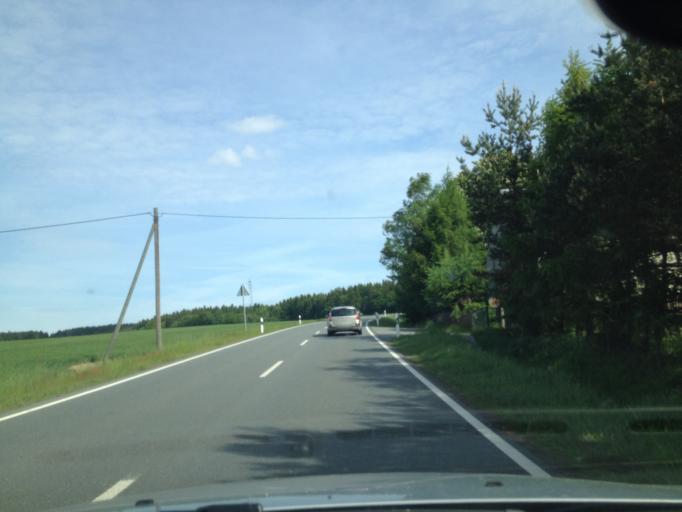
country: DE
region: Saxony
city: Thum
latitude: 50.6844
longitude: 12.9418
